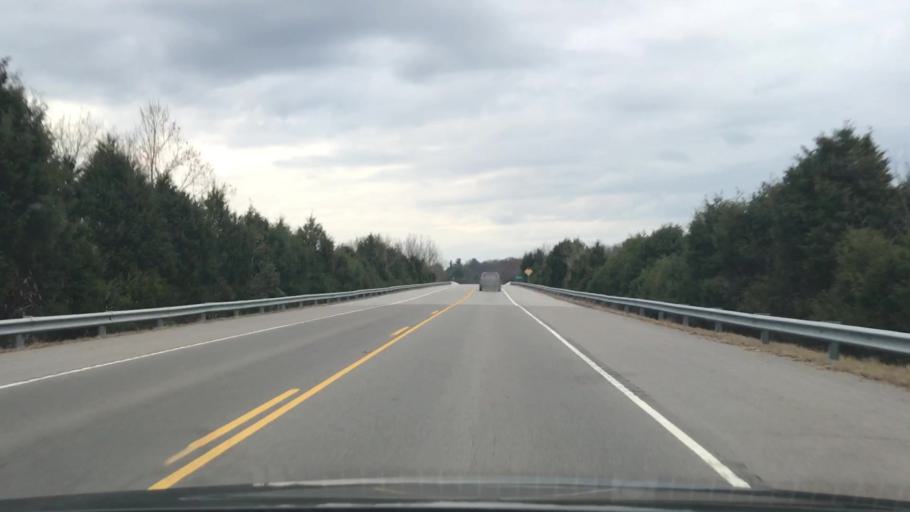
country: US
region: Tennessee
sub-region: Trousdale County
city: Hartsville
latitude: 36.3703
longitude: -86.1759
